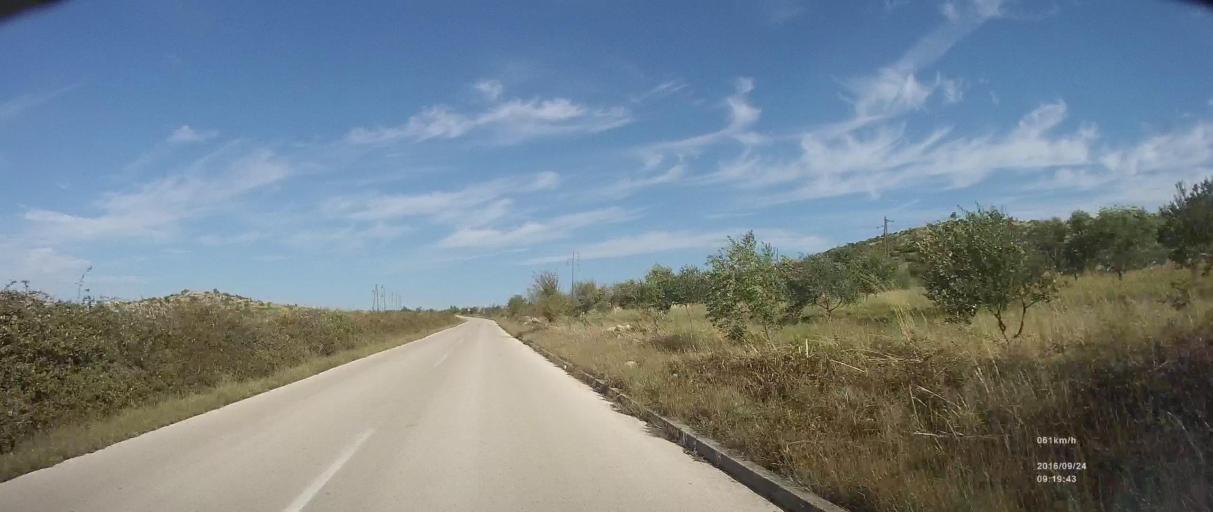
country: HR
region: Zadarska
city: Polaca
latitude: 44.0639
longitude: 15.5023
